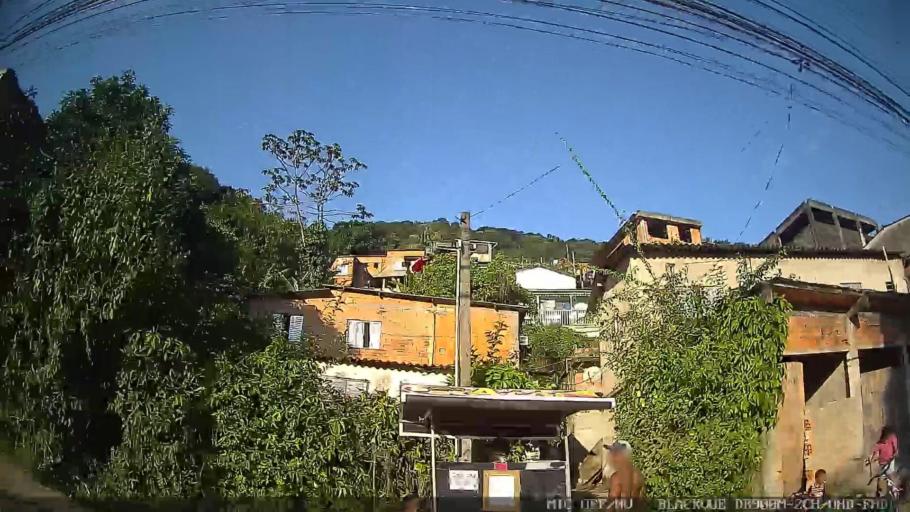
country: BR
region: Sao Paulo
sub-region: Guaruja
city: Guaruja
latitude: -23.9822
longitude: -46.2617
